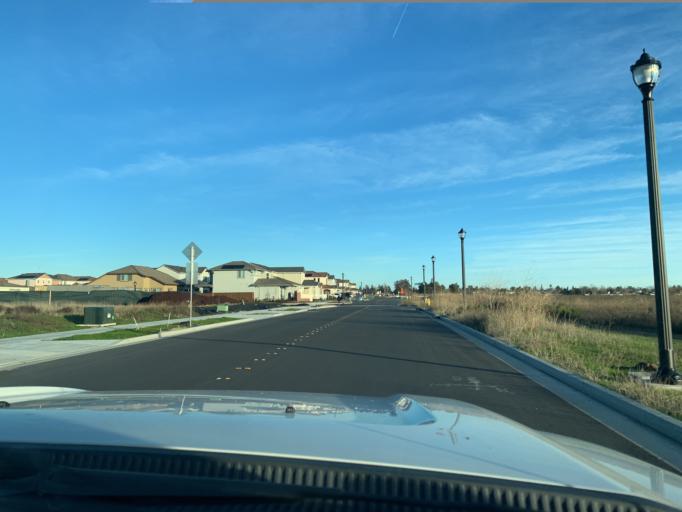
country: US
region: California
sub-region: Yolo County
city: Woodland
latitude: 38.6560
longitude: -121.7472
